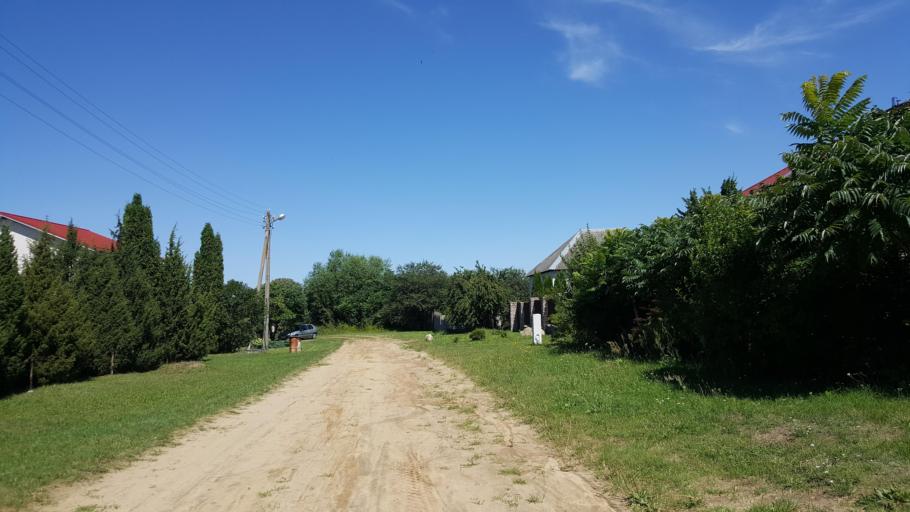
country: BY
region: Brest
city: Charnawchytsy
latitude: 52.2123
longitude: 23.7355
